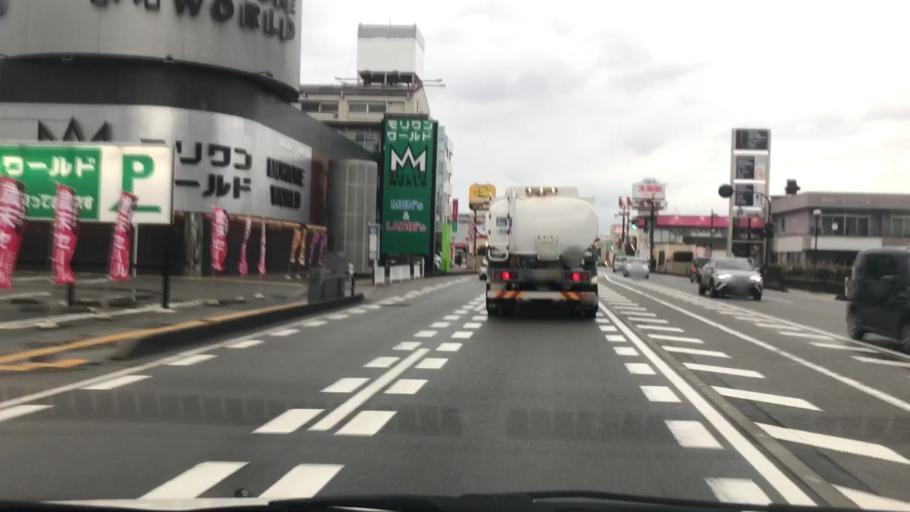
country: JP
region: Toyama
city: Toyama-shi
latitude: 36.6730
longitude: 137.2106
